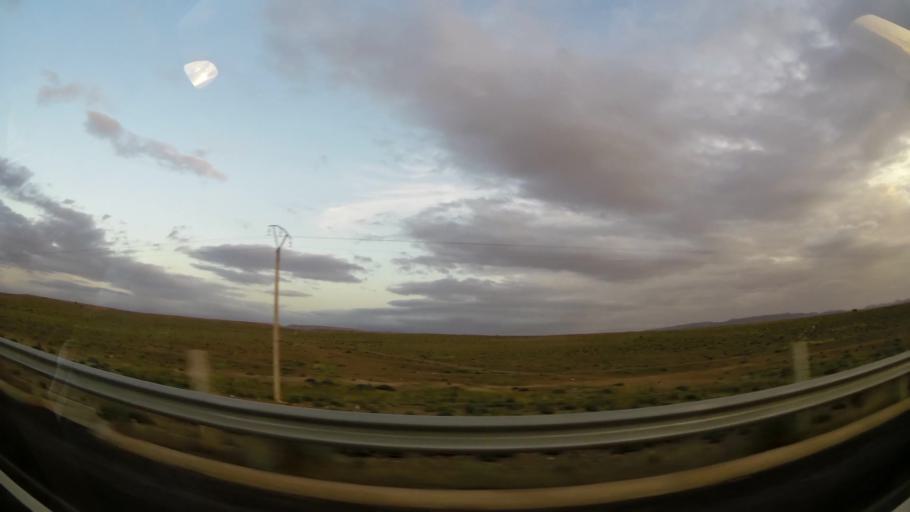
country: MA
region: Oriental
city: Taourirt
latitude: 34.5489
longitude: -2.8854
